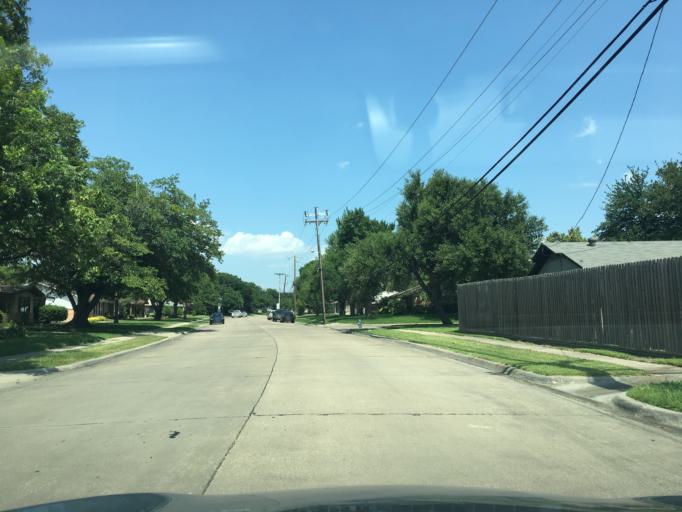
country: US
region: Texas
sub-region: Dallas County
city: Farmers Branch
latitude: 32.9192
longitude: -96.8645
